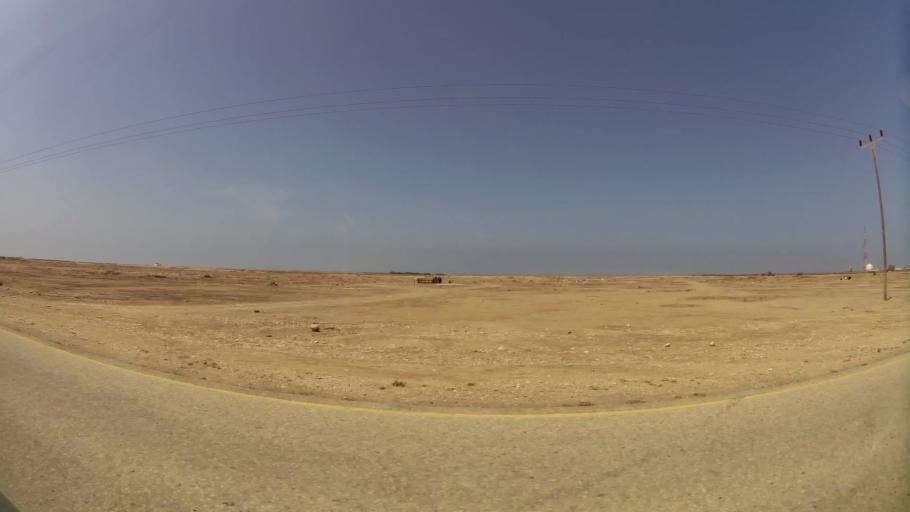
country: OM
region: Zufar
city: Salalah
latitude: 17.0374
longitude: 54.2659
